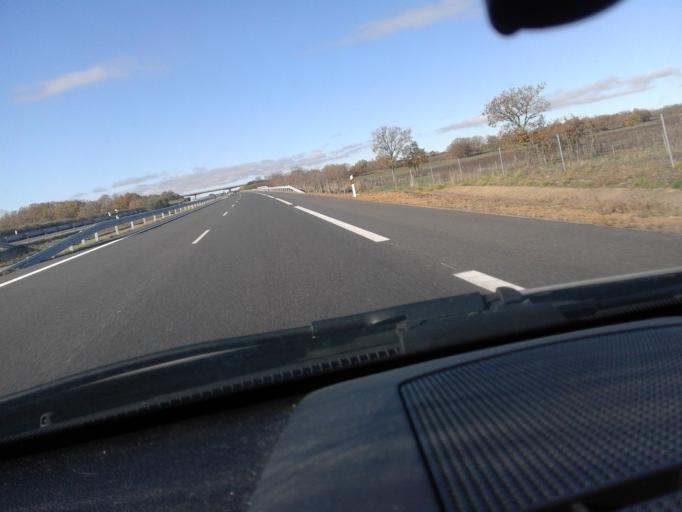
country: ES
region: Castille and Leon
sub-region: Provincia de Palencia
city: Bustillo del Paramo de Carrion
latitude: 42.3580
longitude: -4.7861
